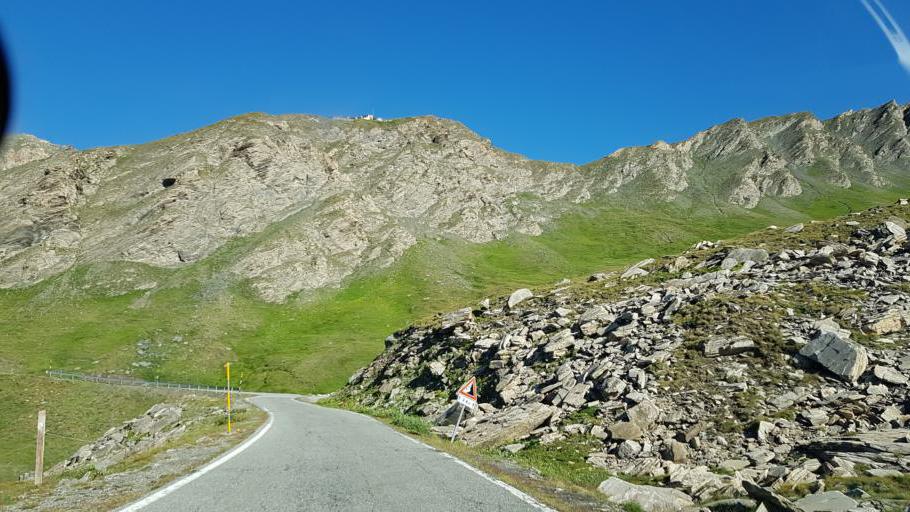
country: IT
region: Piedmont
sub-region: Provincia di Cuneo
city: Pontechianale
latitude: 44.6801
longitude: 6.9846
